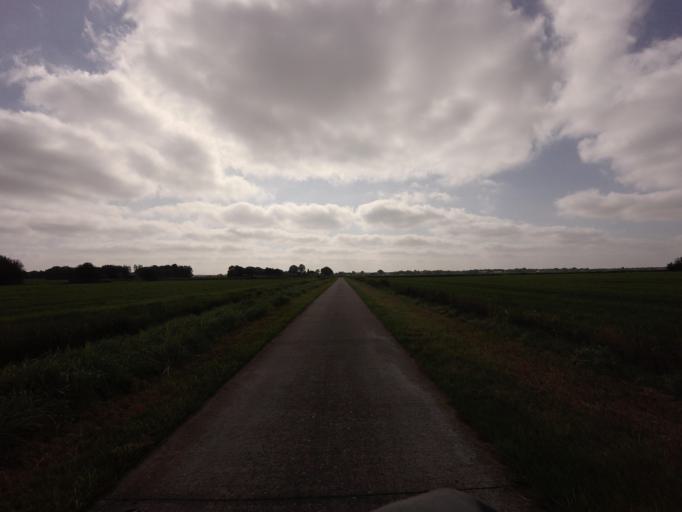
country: NL
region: Overijssel
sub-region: Gemeente Steenwijkerland
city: Steenwijk
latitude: 52.8120
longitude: 6.1764
